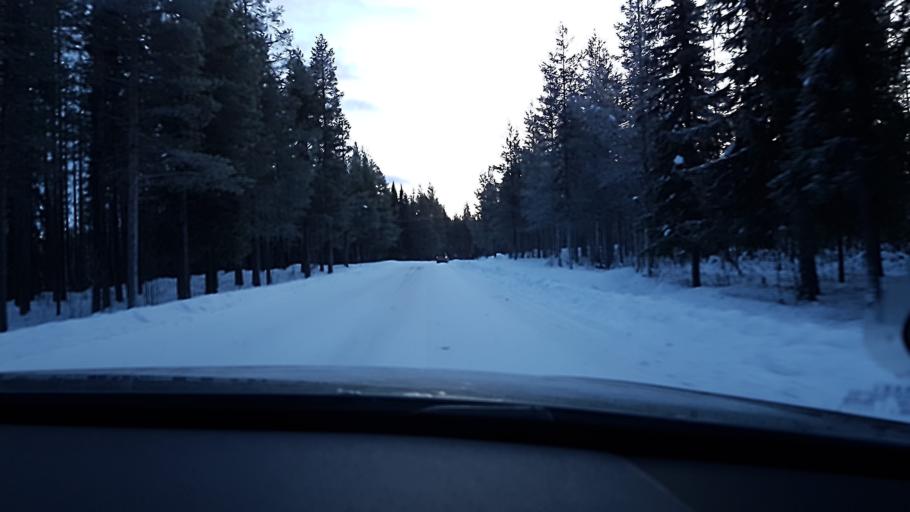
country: SE
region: Vaesterbotten
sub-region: Sorsele Kommun
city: Sorsele
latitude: 65.4987
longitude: 17.5565
